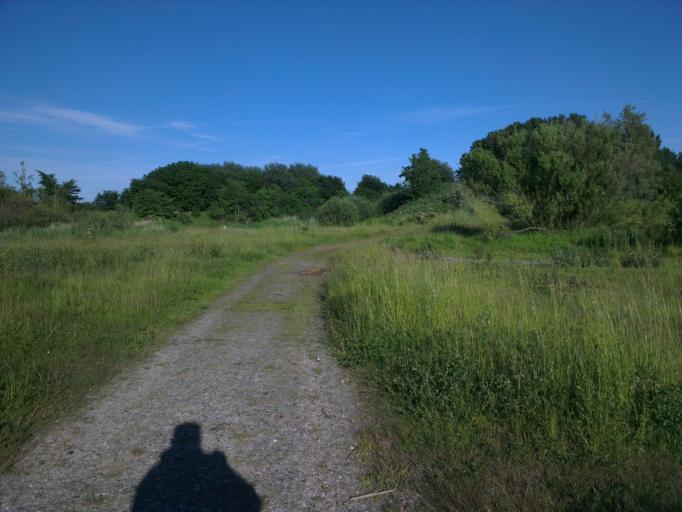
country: DK
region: Capital Region
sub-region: Frederikssund Kommune
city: Skibby
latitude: 55.7675
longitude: 12.0282
